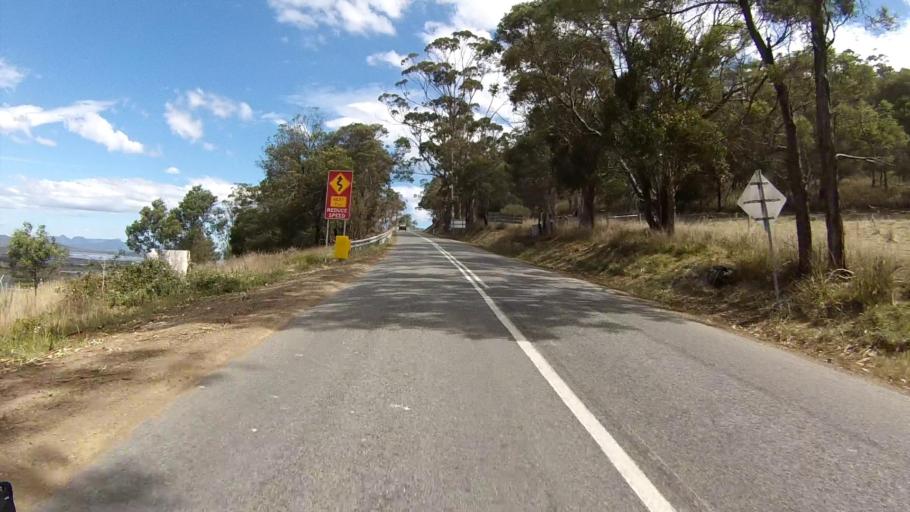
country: AU
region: Tasmania
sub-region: Break O'Day
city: St Helens
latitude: -41.9719
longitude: 148.1509
